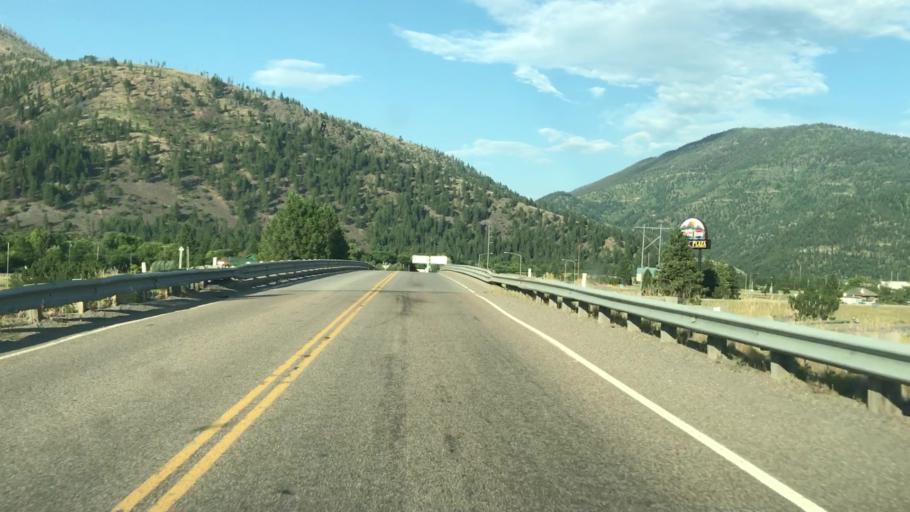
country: US
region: Montana
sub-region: Missoula County
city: Bonner-West Riverside
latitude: 46.8765
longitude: -113.8942
